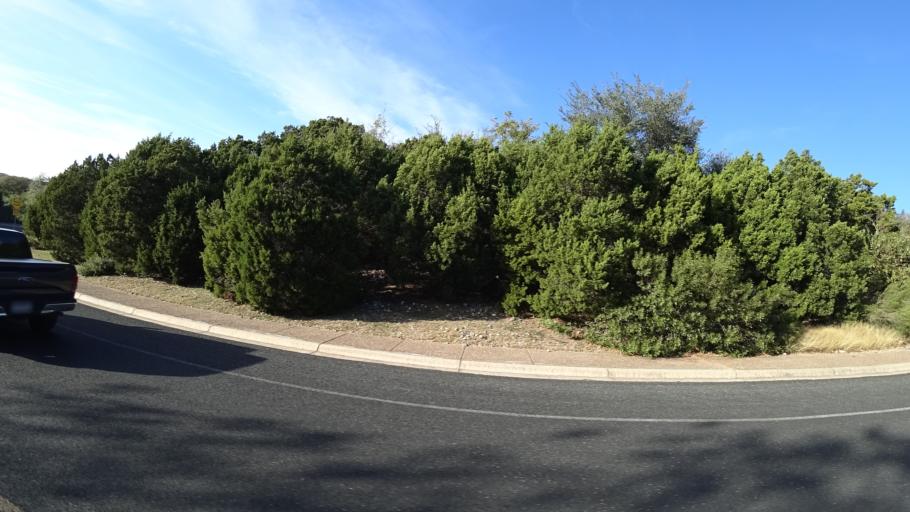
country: US
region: Texas
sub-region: Williamson County
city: Jollyville
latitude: 30.4067
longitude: -97.7509
